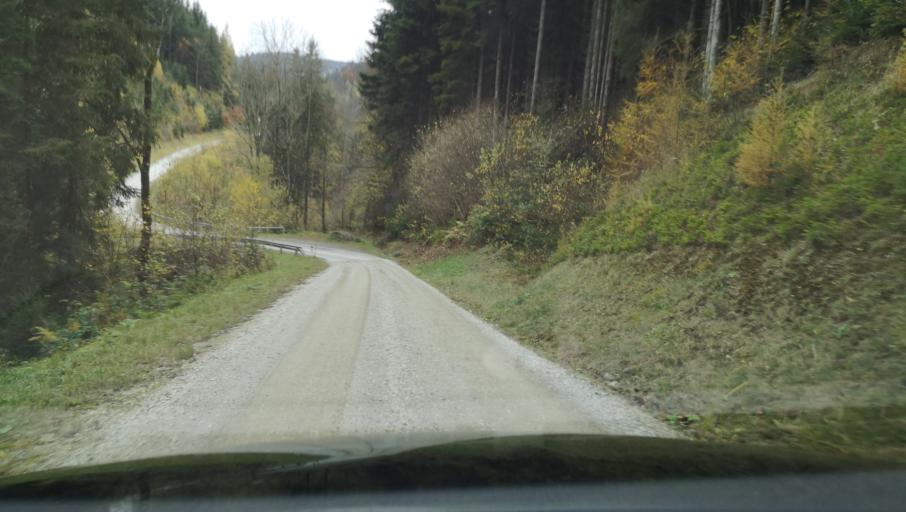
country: AT
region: Styria
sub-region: Politischer Bezirk Weiz
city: Birkfeld
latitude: 47.3728
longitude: 15.6284
